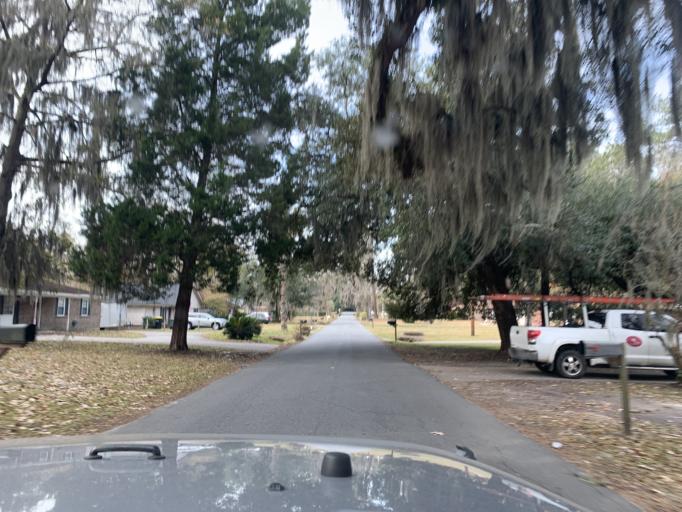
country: US
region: Georgia
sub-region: Chatham County
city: Montgomery
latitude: 31.9686
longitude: -81.1306
